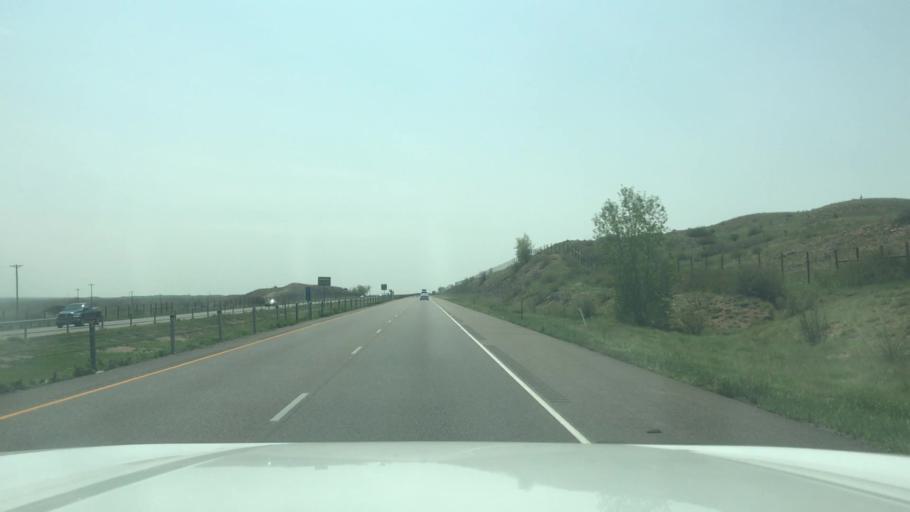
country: US
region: Colorado
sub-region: El Paso County
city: Fountain
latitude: 38.6513
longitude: -104.6970
